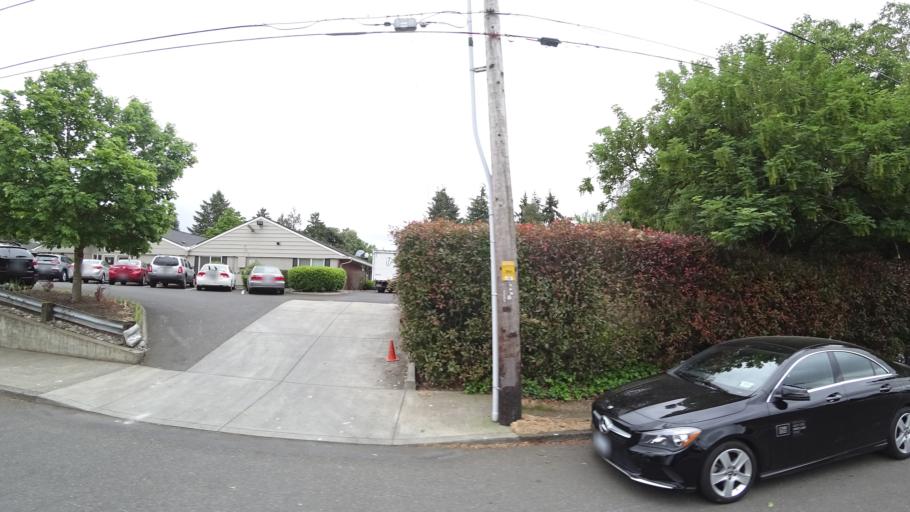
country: US
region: Oregon
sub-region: Multnomah County
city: Portland
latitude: 45.5555
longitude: -122.6086
